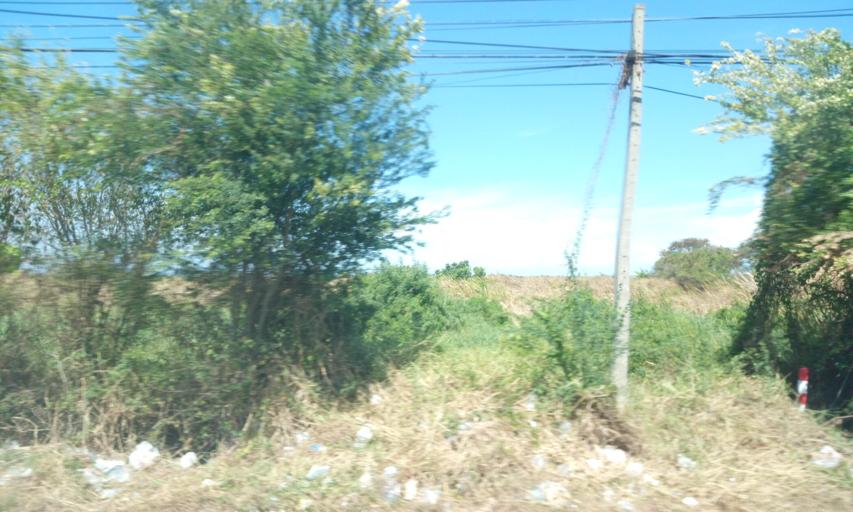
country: TH
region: Samut Prakan
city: Bang Bo District
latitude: 13.5189
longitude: 100.7885
